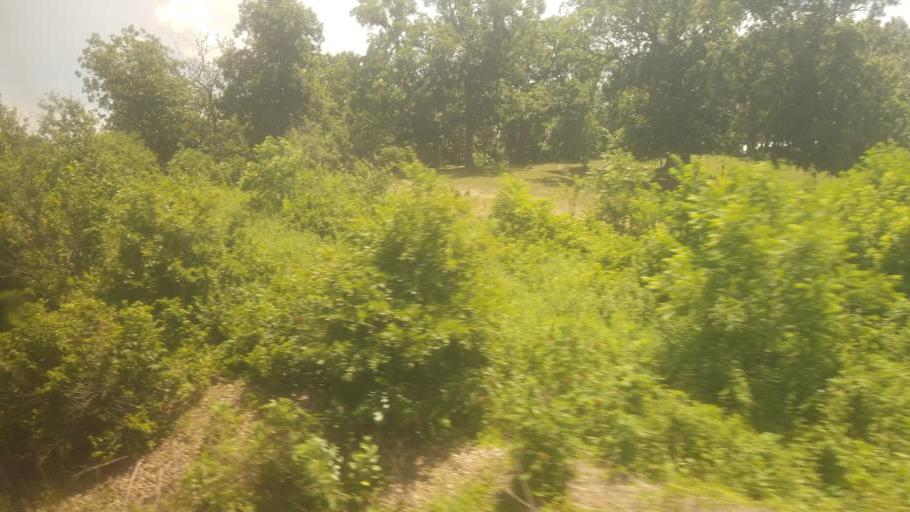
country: US
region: Missouri
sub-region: Linn County
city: Marceline
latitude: 39.8609
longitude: -92.8046
